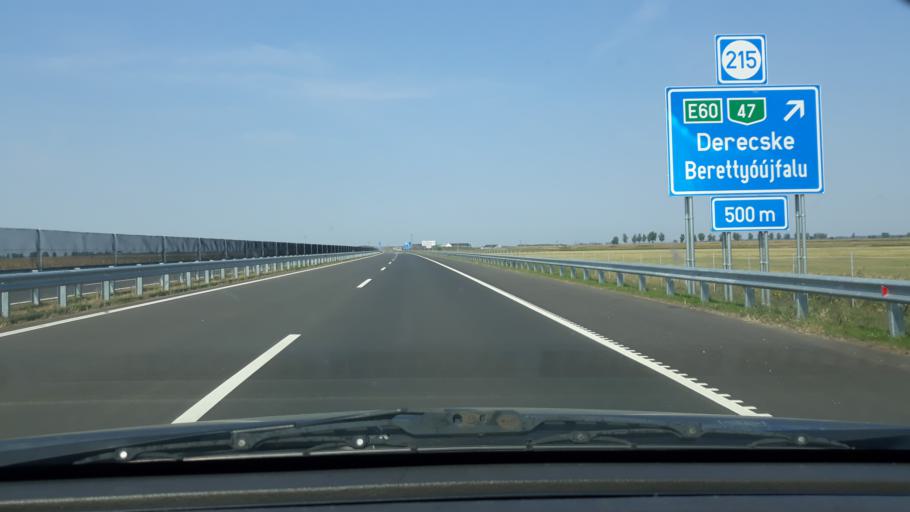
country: HU
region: Hajdu-Bihar
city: Berettyoujfalu
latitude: 47.2684
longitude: 21.5576
